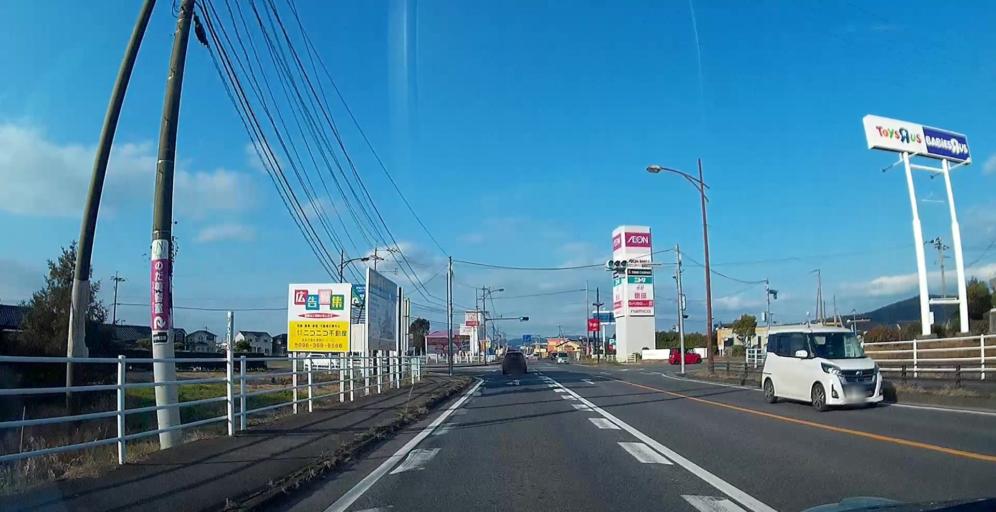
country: JP
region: Kumamoto
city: Matsubase
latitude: 32.5978
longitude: 130.7024
